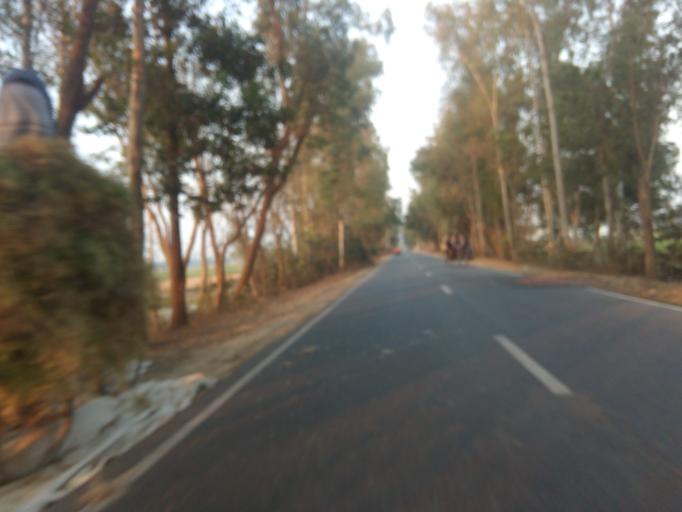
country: BD
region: Rajshahi
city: Bogra
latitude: 24.6323
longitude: 89.2468
